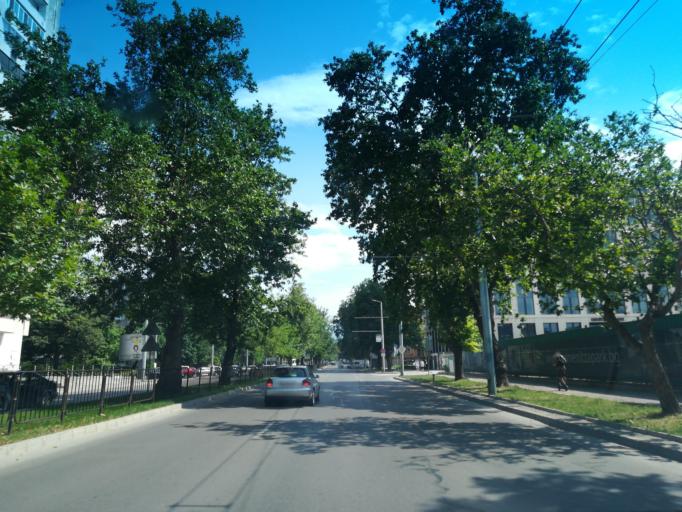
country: BG
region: Plovdiv
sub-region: Obshtina Plovdiv
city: Plovdiv
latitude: 42.1435
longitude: 24.7631
